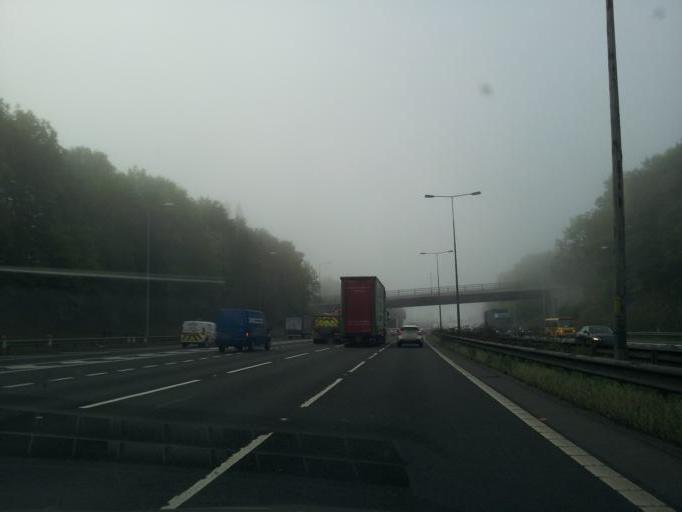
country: GB
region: England
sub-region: Kirklees
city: Cleckheaton
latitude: 53.7299
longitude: -1.7320
